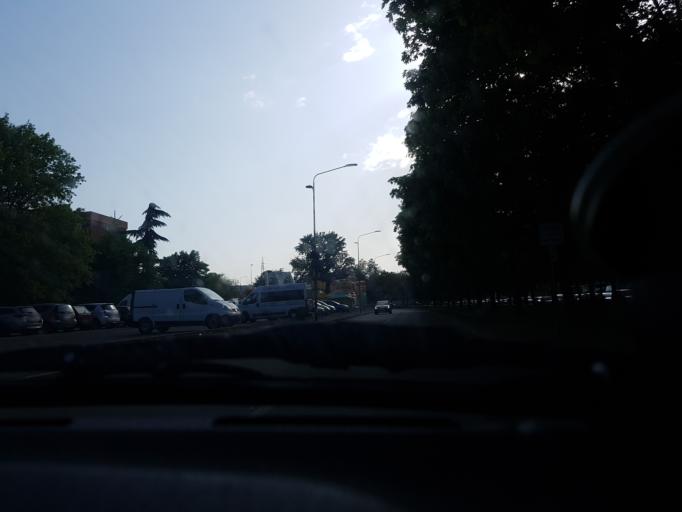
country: IT
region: Lombardy
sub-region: Citta metropolitana di Milano
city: Cesano Boscone
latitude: 45.4564
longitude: 9.0932
